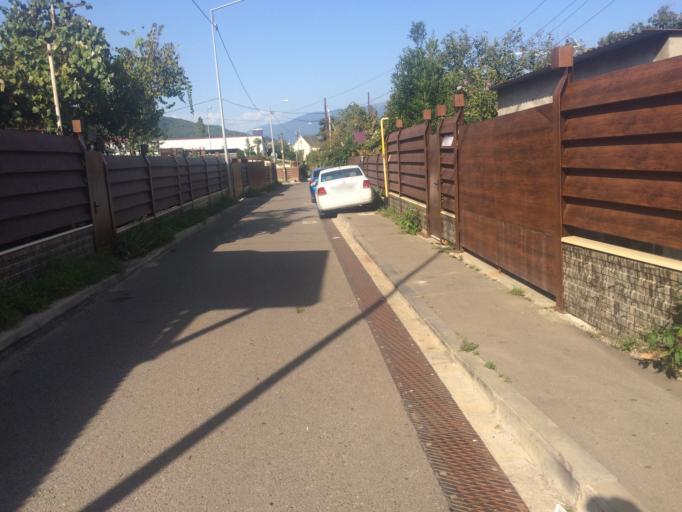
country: RU
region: Krasnodarskiy
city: Adler
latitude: 43.3922
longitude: 39.9844
